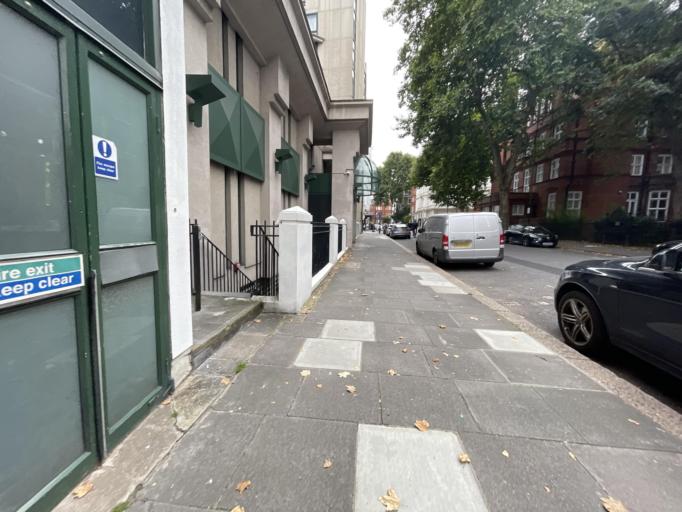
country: GB
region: England
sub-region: Greater London
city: Kensington
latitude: 51.4936
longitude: -0.1842
